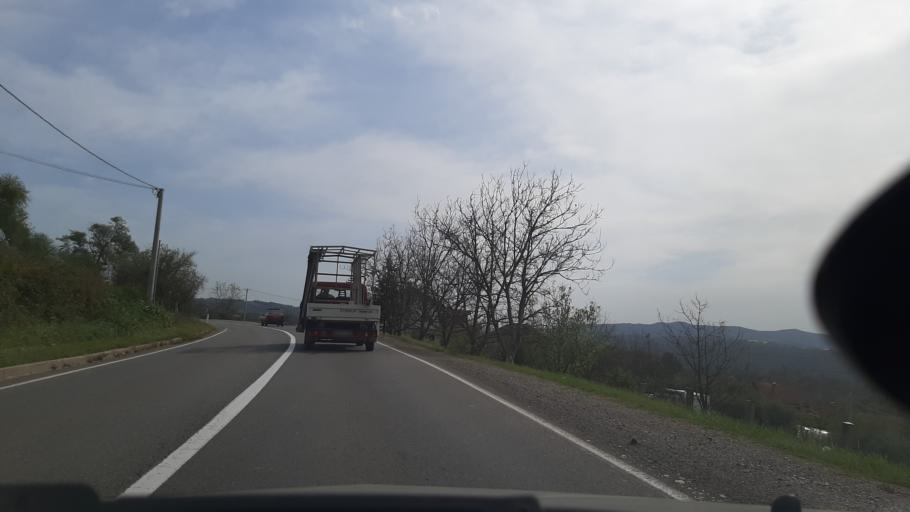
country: BA
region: Republika Srpska
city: Laktasi
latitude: 44.8675
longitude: 17.3408
